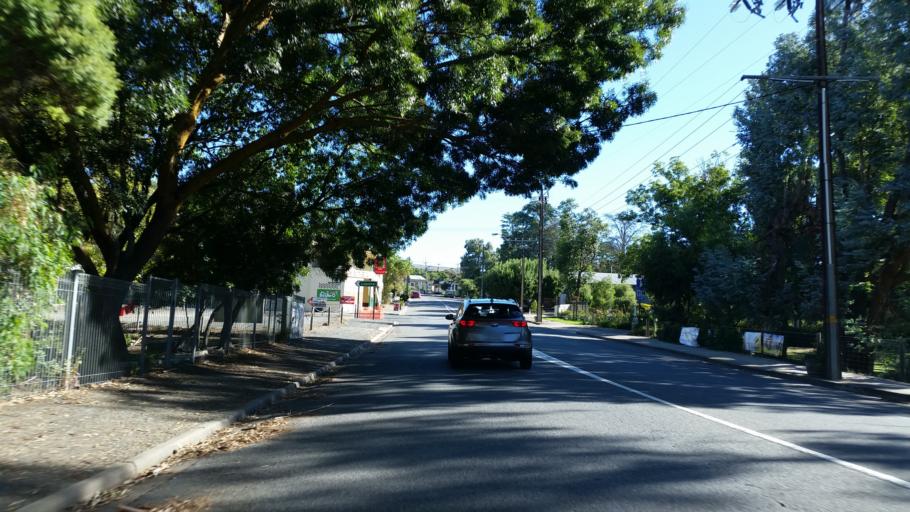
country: AU
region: South Australia
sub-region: Adelaide Hills
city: Gumeracha
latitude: -34.8232
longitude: 138.8853
